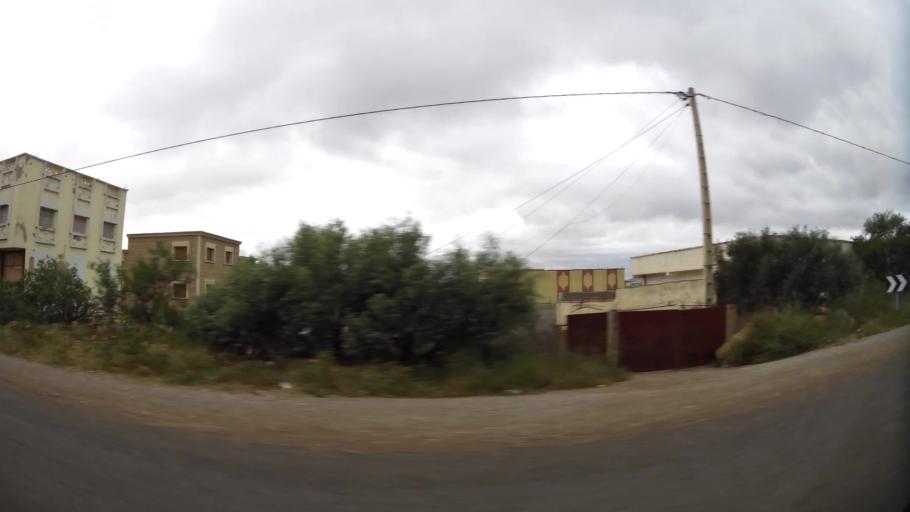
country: MA
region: Oriental
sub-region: Nador
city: Midar
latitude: 35.0583
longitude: -3.4674
